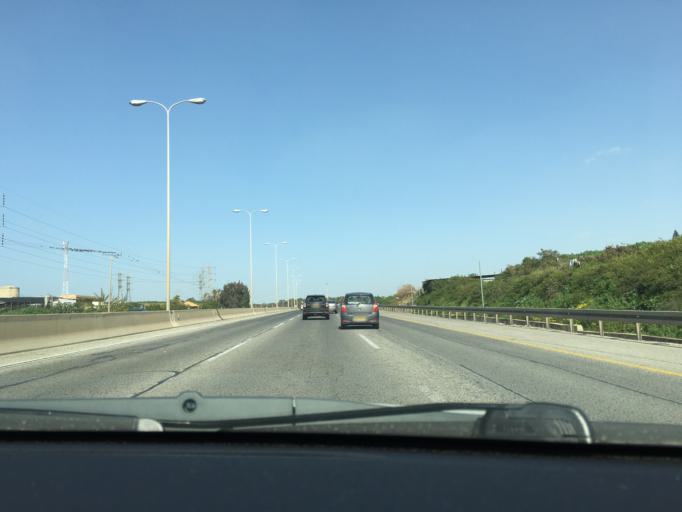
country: IL
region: Central District
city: Hod HaSharon
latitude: 32.1418
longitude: 34.8733
